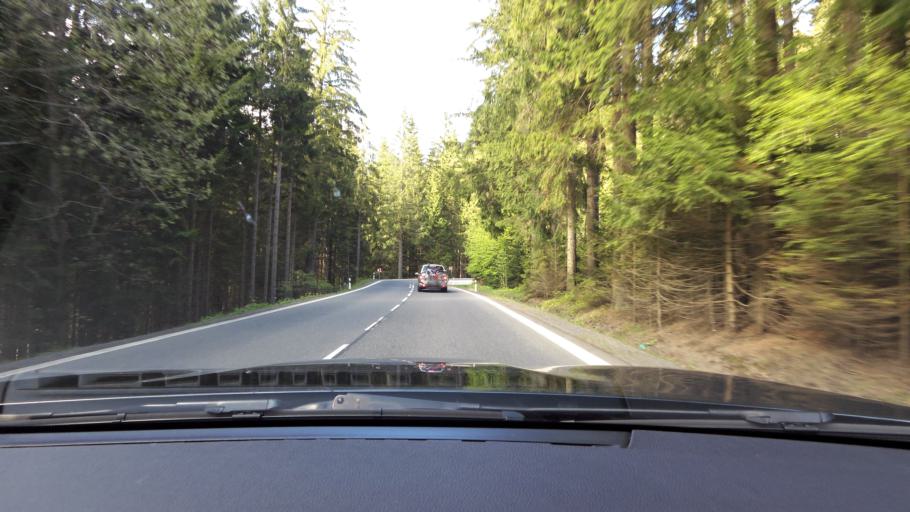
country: CZ
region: Plzensky
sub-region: Okres Klatovy
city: Zelezna Ruda
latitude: 49.2097
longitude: 13.3073
